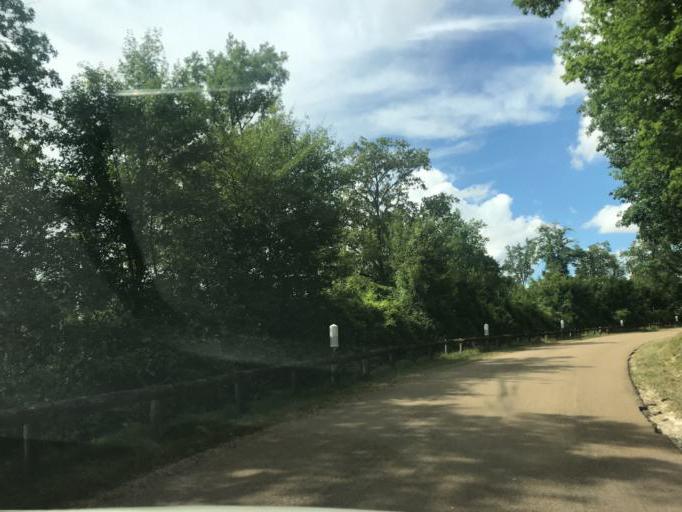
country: FR
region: Bourgogne
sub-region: Departement de l'Yonne
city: Fontenailles
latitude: 47.5608
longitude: 3.3392
